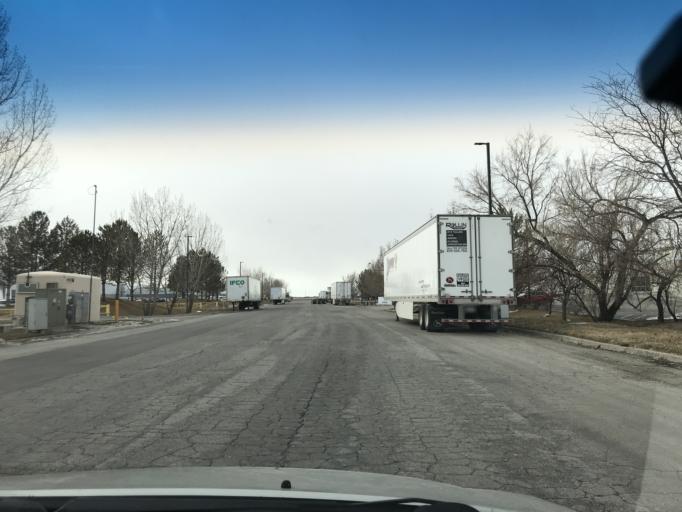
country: US
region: Utah
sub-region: Salt Lake County
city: West Valley City
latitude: 40.7788
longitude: -112.0314
